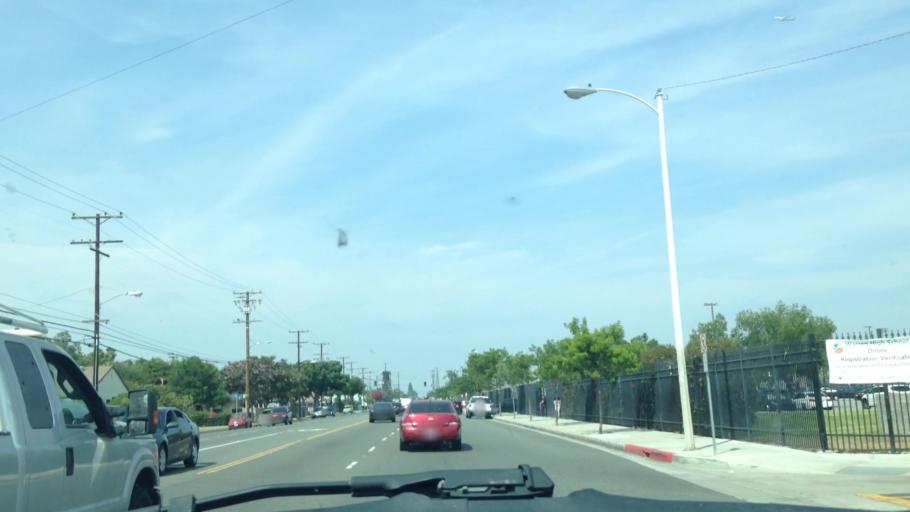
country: US
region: California
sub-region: Los Angeles County
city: Downey
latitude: 33.9358
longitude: -118.1430
